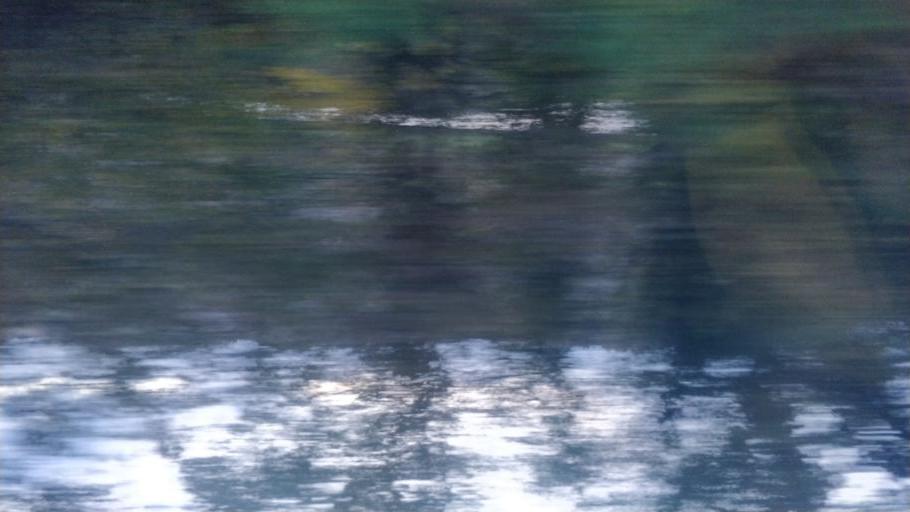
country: GB
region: England
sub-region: Borough of Wigan
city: Shevington
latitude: 53.5667
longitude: -2.7086
